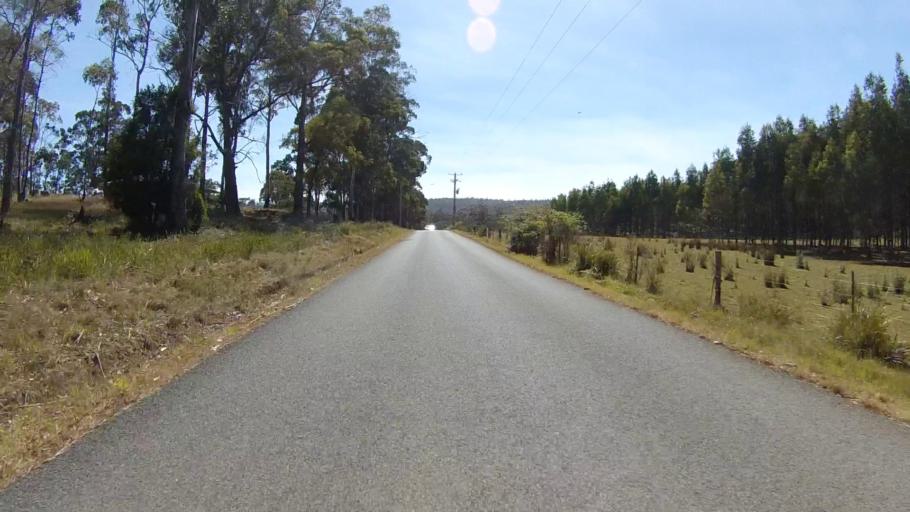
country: AU
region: Tasmania
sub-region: Sorell
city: Sorell
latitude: -42.7501
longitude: 147.7160
